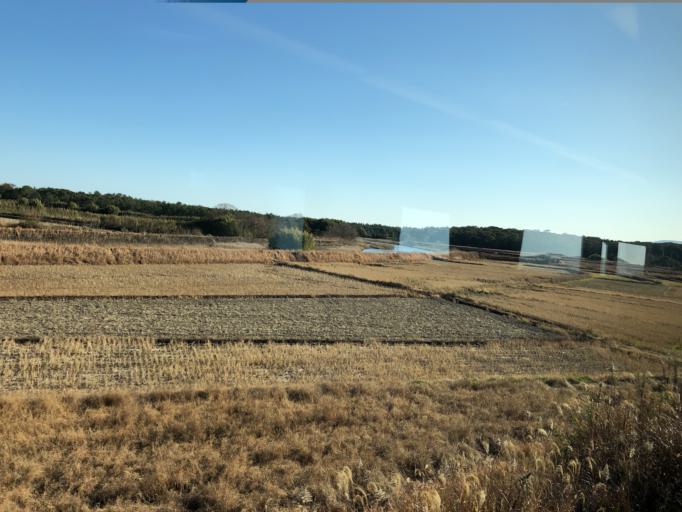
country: JP
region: Kochi
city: Nakamura
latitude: 33.0348
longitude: 133.0195
